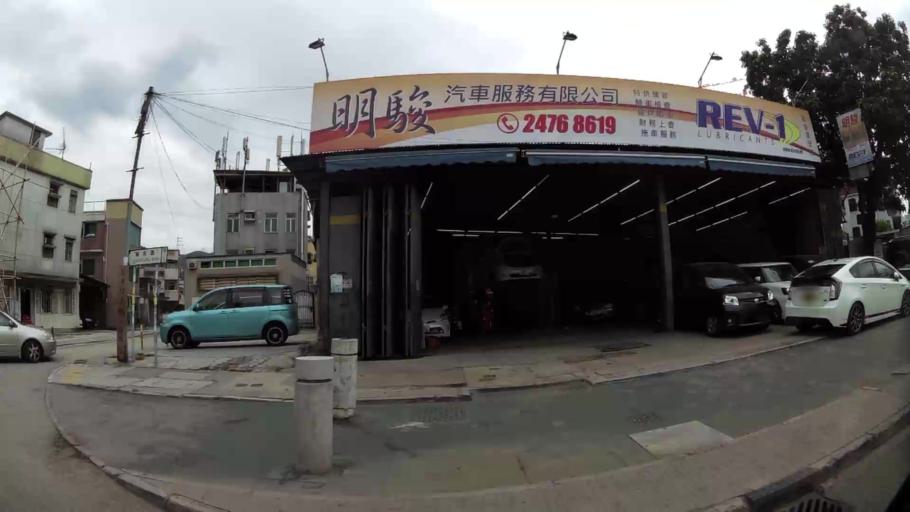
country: HK
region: Tuen Mun
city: Tuen Mun
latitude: 22.4247
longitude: 113.9878
